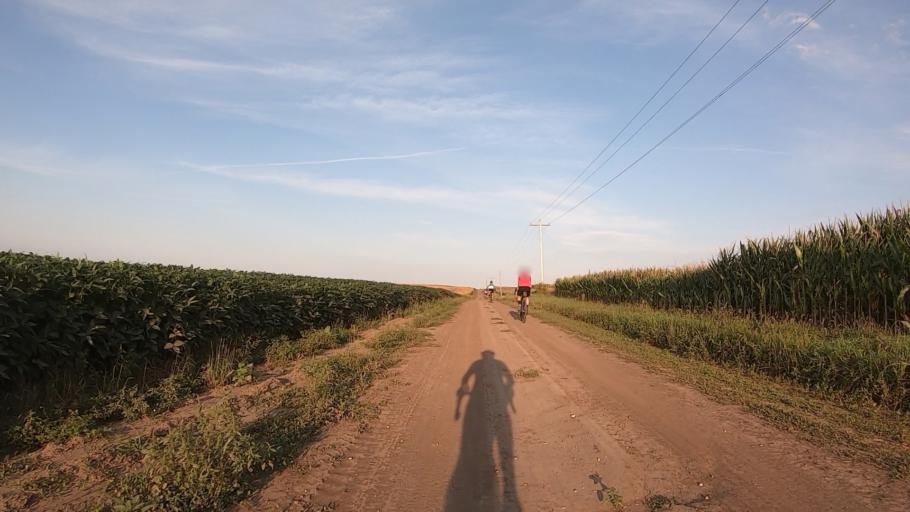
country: US
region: Kansas
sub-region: Marshall County
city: Marysville
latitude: 39.7695
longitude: -96.7219
